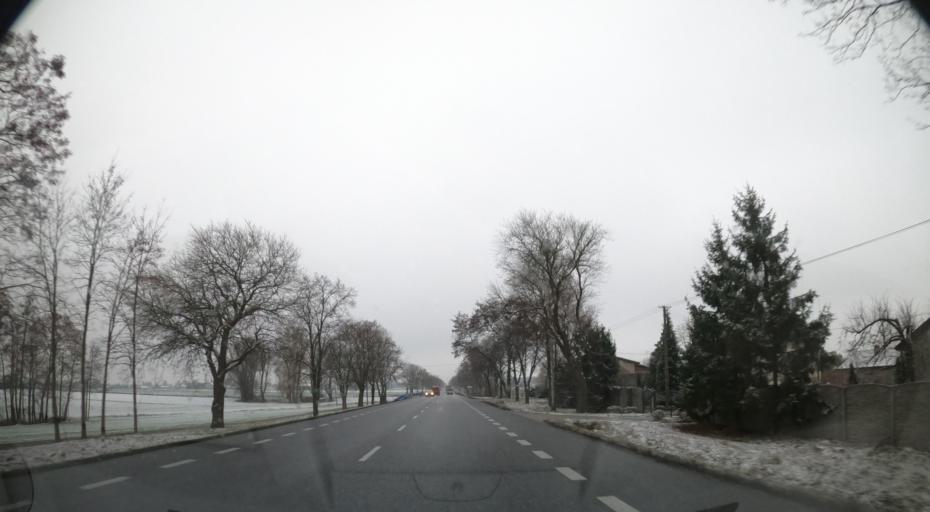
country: PL
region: Masovian Voivodeship
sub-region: Powiat warszawski zachodni
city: Bieniewice
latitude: 52.2018
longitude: 20.5402
